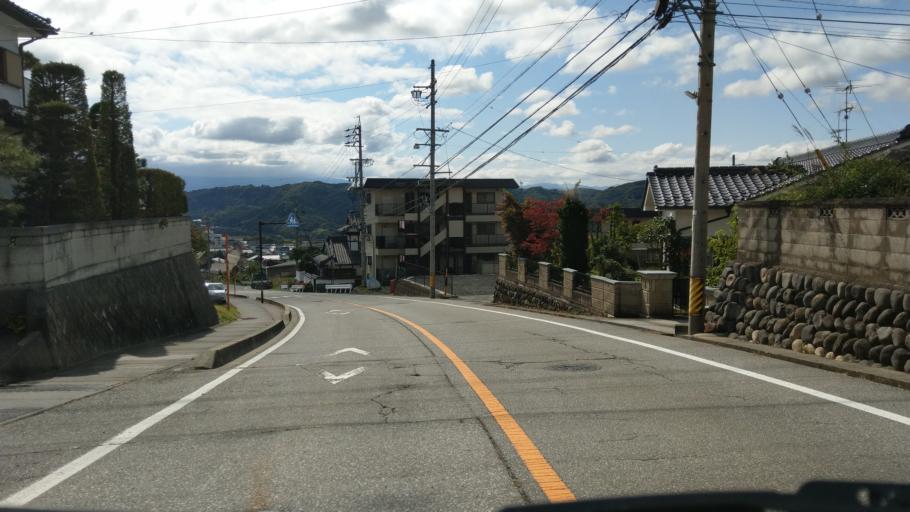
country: JP
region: Nagano
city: Komoro
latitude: 36.3357
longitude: 138.4266
